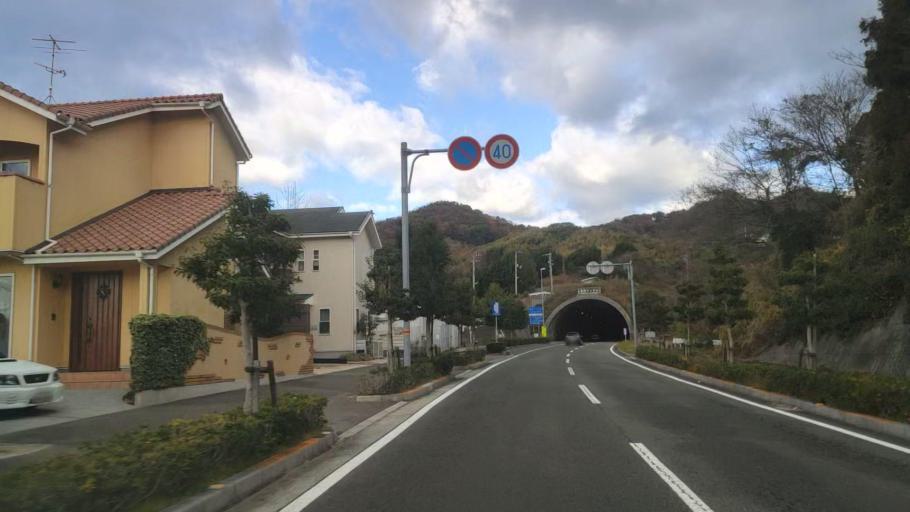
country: JP
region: Ehime
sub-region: Shikoku-chuo Shi
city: Matsuyama
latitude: 33.8751
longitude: 132.7150
